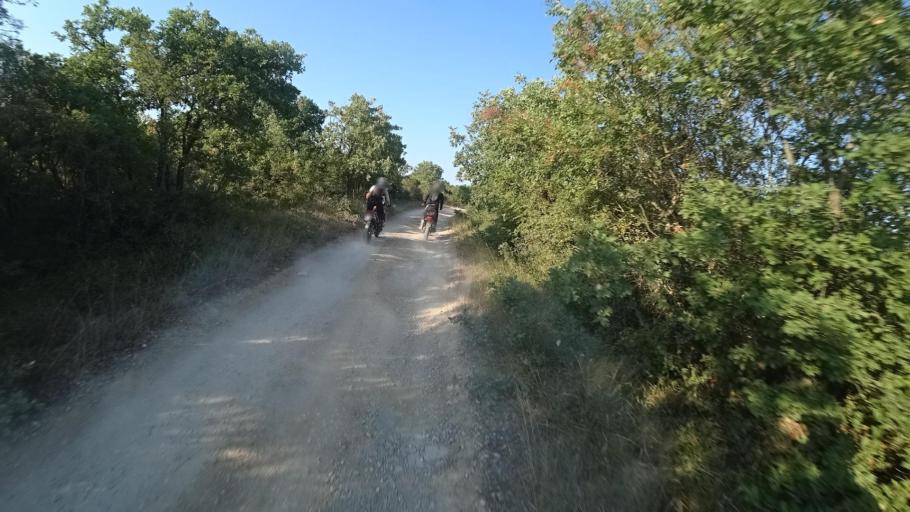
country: HR
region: Istarska
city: Galizana
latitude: 44.9181
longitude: 13.8709
